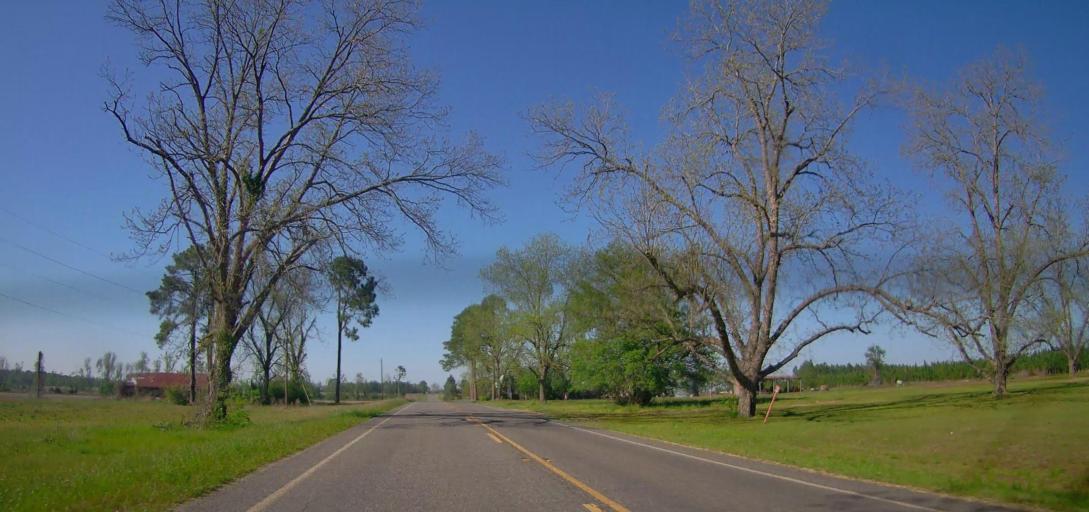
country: US
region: Georgia
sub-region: Wilcox County
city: Rochelle
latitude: 31.9654
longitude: -83.4563
